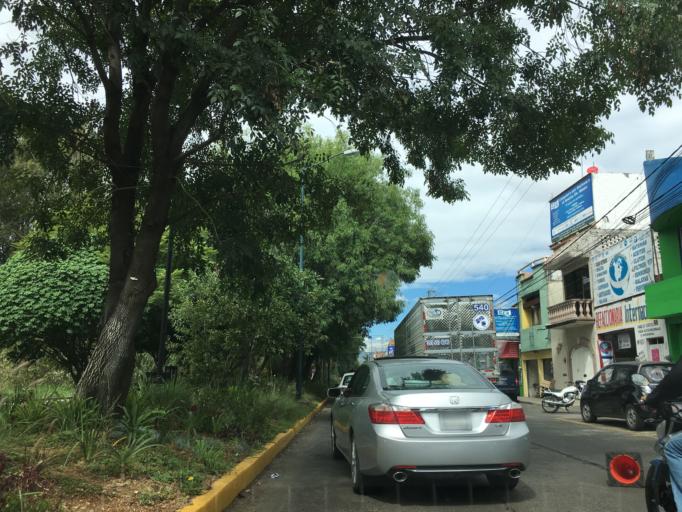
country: MX
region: Michoacan
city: Morelia
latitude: 19.6891
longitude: -101.1831
